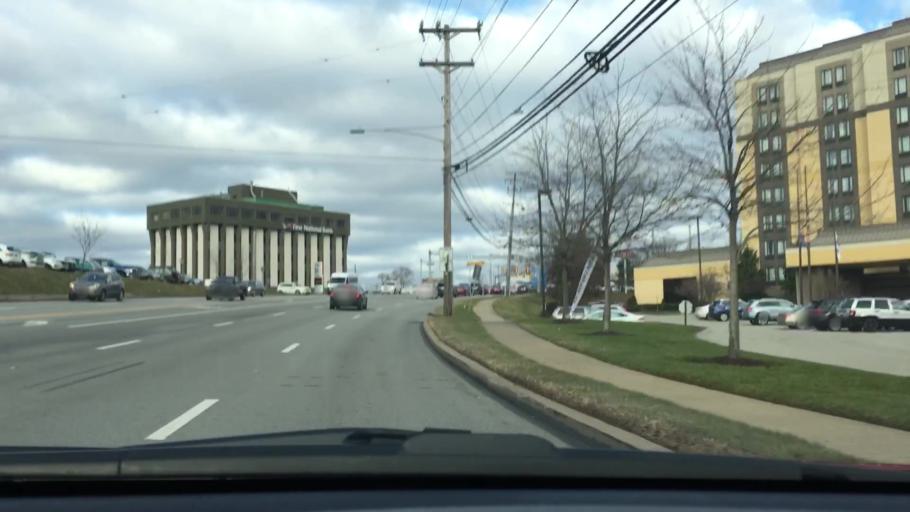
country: US
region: Pennsylvania
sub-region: Allegheny County
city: Monroeville
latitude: 40.4375
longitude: -79.7592
